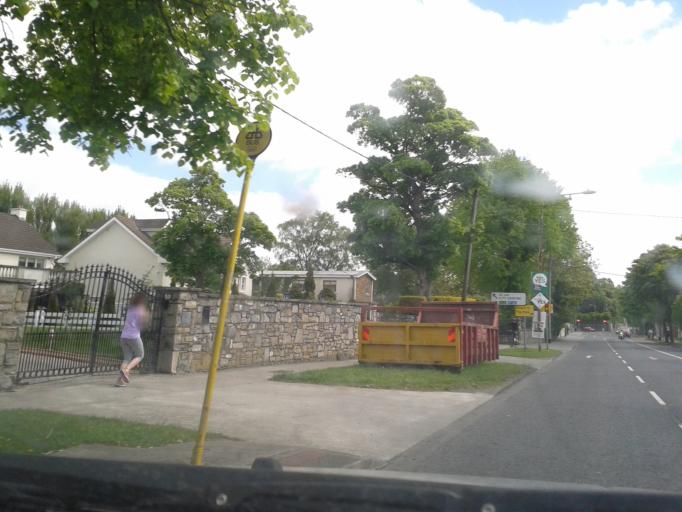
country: IE
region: Leinster
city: Castleknock
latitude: 53.3706
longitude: -6.3516
